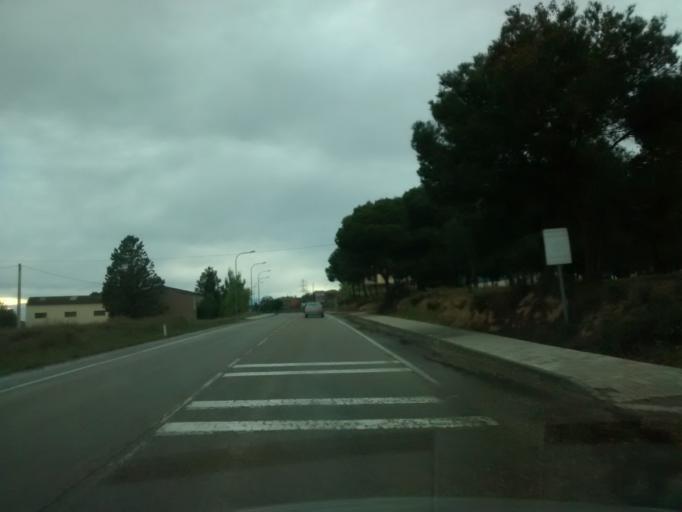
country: ES
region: Aragon
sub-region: Provincia de Zaragoza
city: Caspe
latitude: 41.2250
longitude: -0.0273
